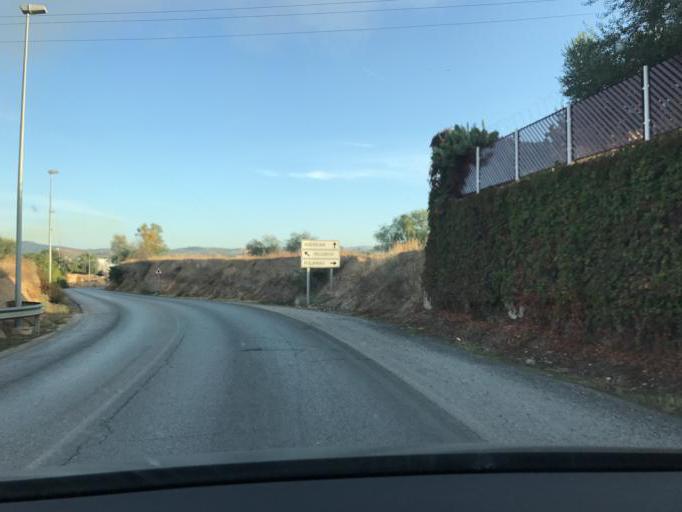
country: ES
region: Andalusia
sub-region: Provincia de Granada
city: Pulianas
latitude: 37.2250
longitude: -3.6098
